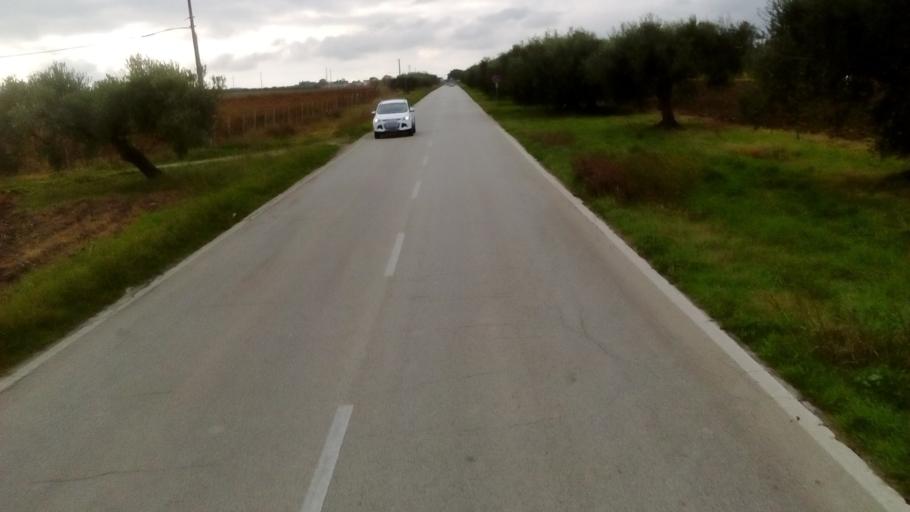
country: IT
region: Abruzzo
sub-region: Provincia di Chieti
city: Vasto
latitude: 42.1559
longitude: 14.7009
